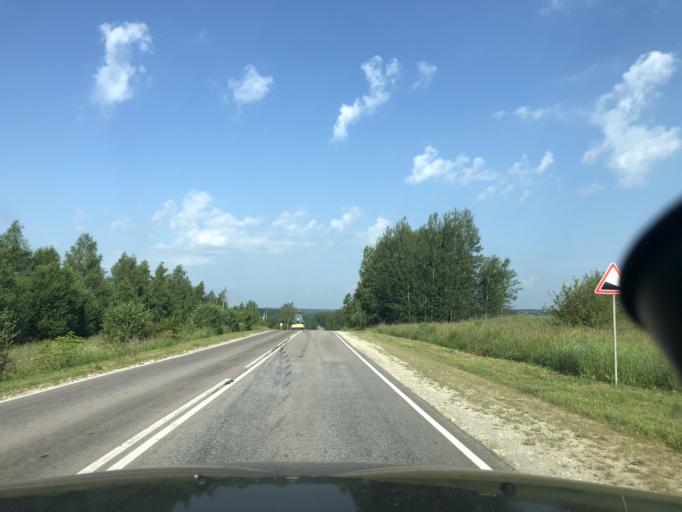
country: RU
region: Tula
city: Dubna
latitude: 54.1430
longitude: 36.9992
